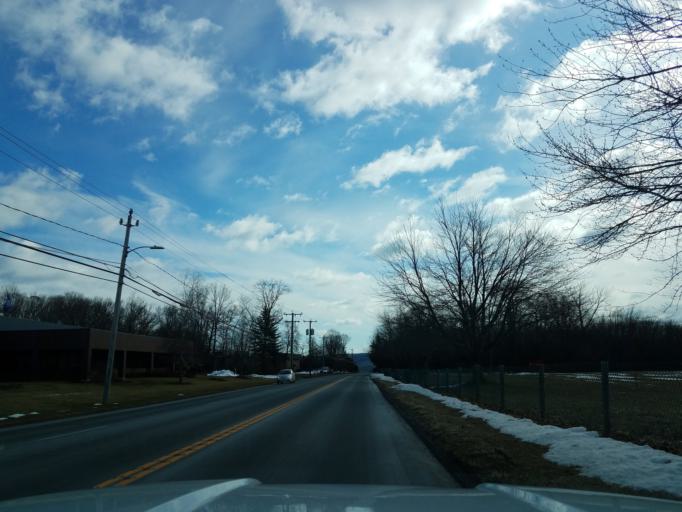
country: US
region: Connecticut
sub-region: Hartford County
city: Plainville
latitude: 41.6390
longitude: -72.8946
